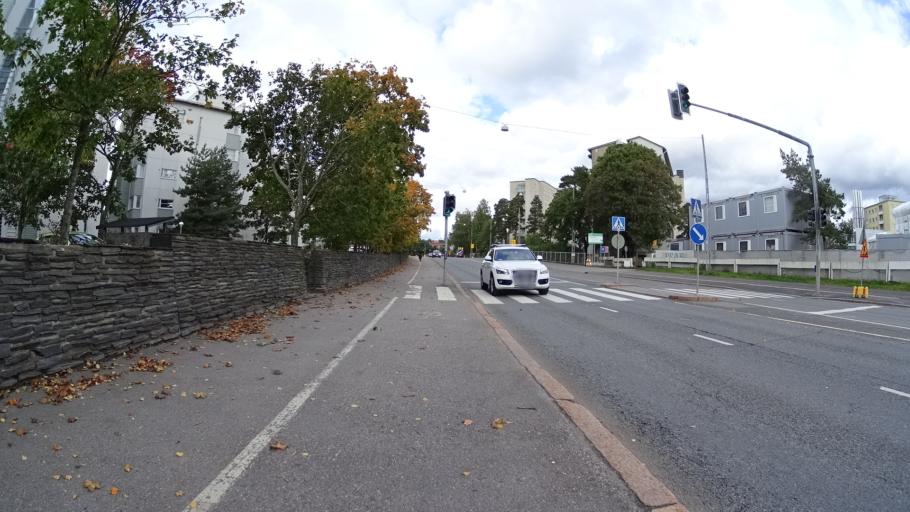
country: FI
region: Uusimaa
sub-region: Helsinki
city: Helsinki
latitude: 60.1893
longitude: 24.9025
